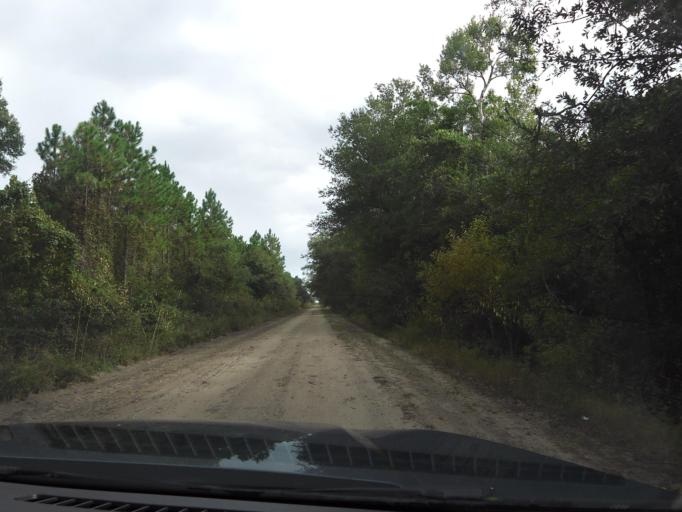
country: US
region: Florida
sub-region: Flagler County
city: Palm Coast
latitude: 29.5722
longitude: -81.3390
